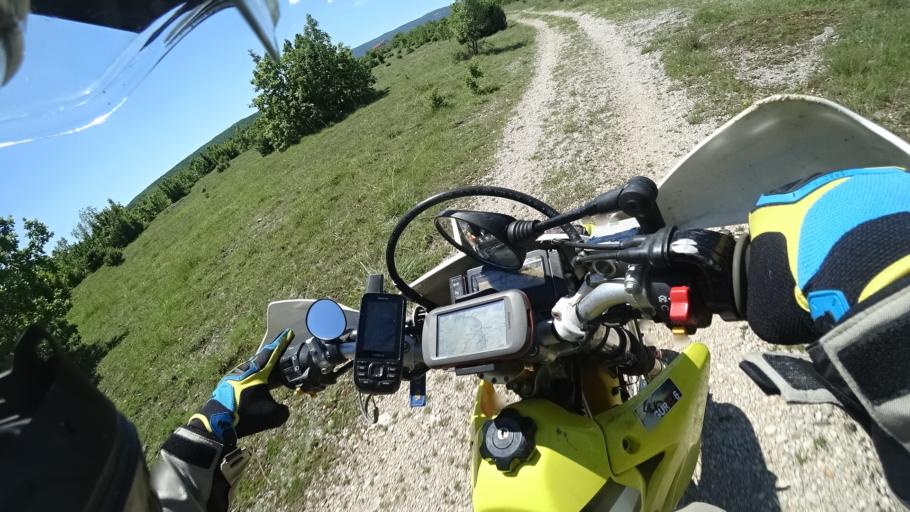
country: HR
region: Sibensko-Kniniska
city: Knin
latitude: 44.0143
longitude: 16.3256
